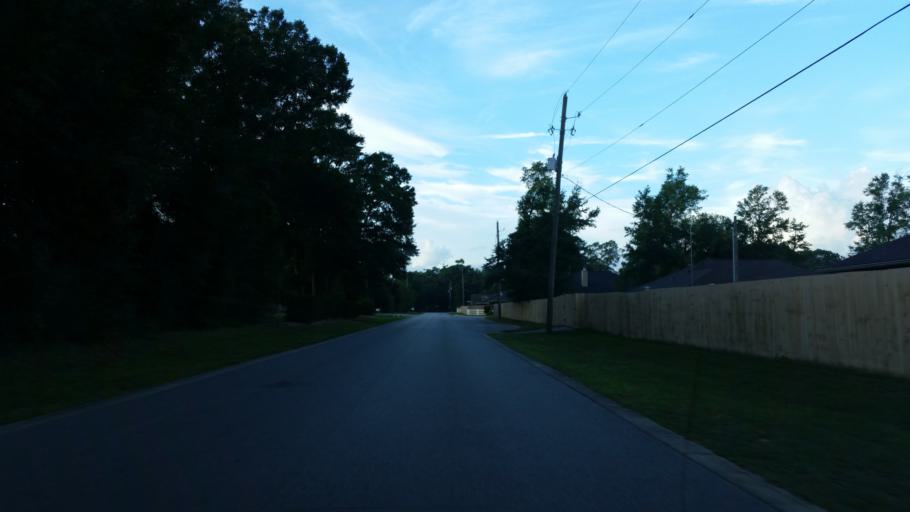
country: US
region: Florida
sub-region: Escambia County
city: Ensley
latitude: 30.5302
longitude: -87.3049
